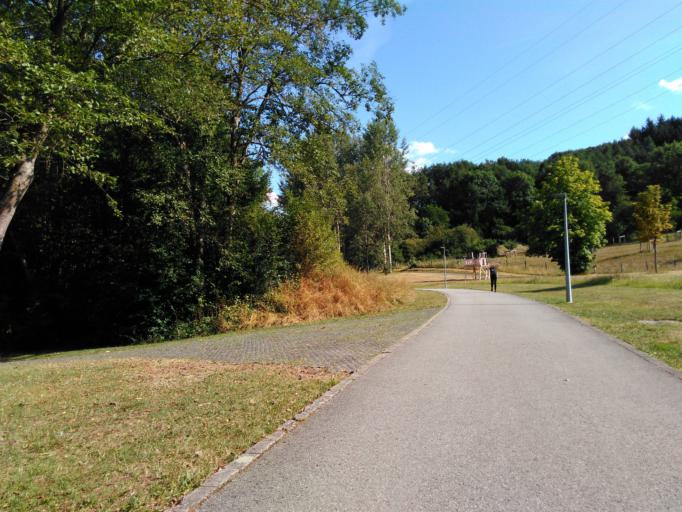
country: LU
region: Grevenmacher
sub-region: Canton d'Echternach
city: Echternach
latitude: 49.7955
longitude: 6.4136
